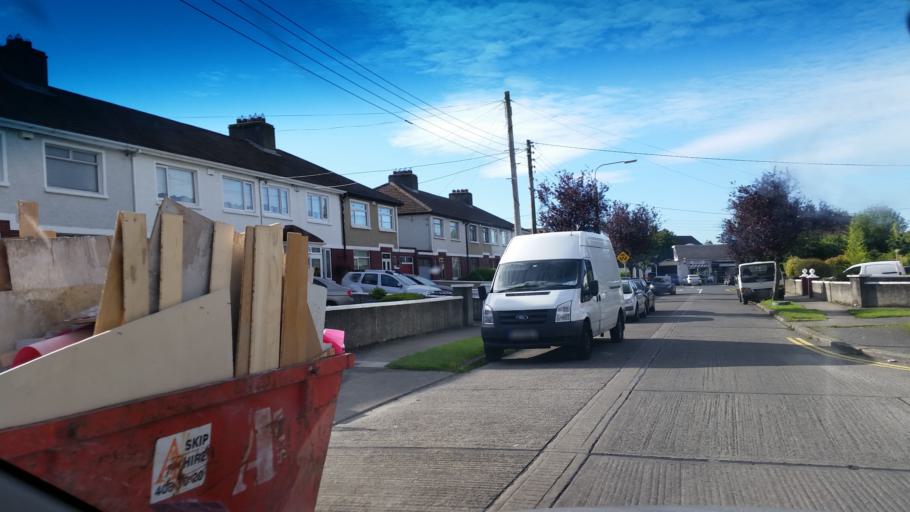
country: IE
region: Leinster
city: Beaumont
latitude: 53.3888
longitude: -6.2373
